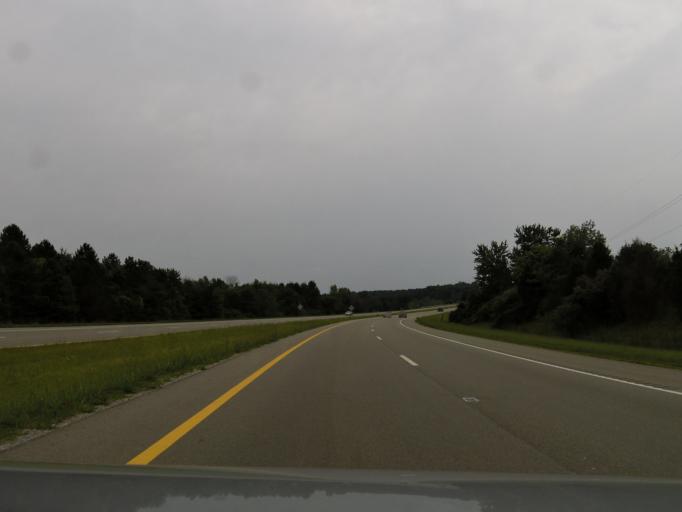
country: US
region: Ohio
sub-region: Warren County
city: Waynesville
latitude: 39.5123
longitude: -84.0293
